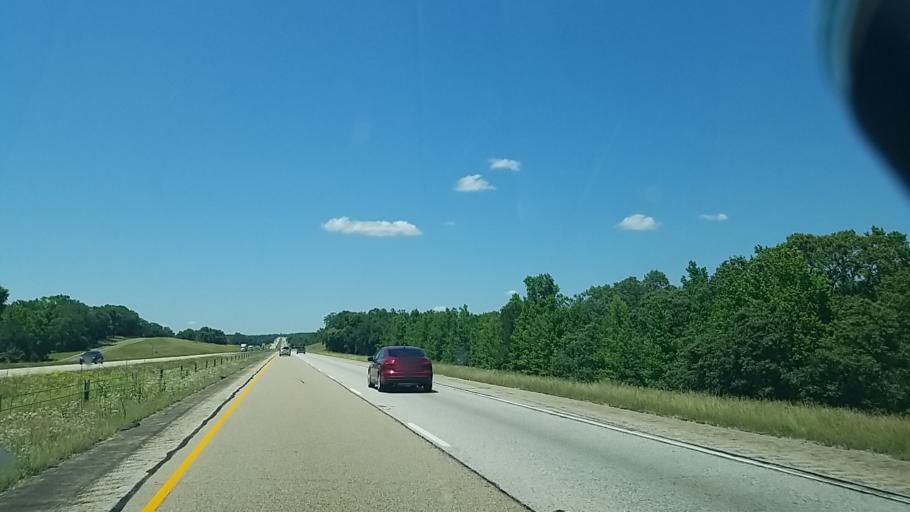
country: US
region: Texas
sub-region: Leon County
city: Centerville
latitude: 31.1747
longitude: -95.9887
